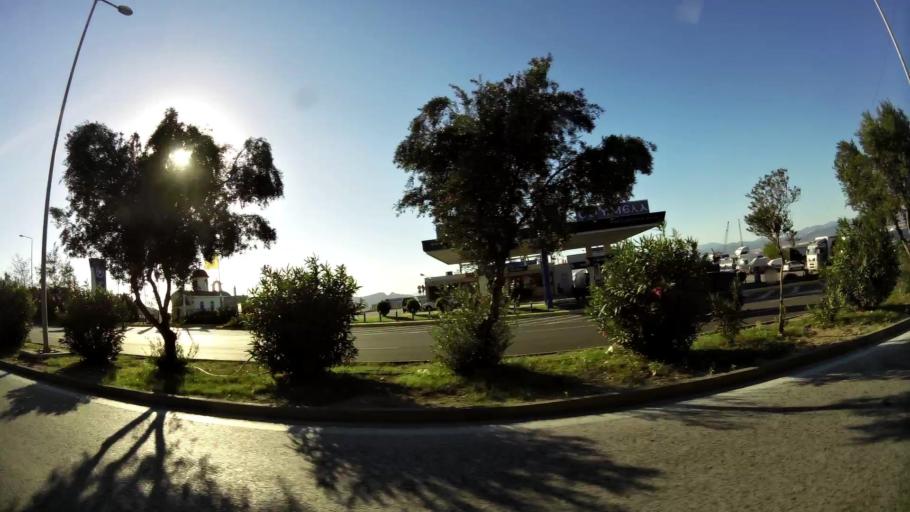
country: GR
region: Attica
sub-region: Nomarchia Athinas
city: Skaramangas
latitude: 38.0062
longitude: 23.6041
